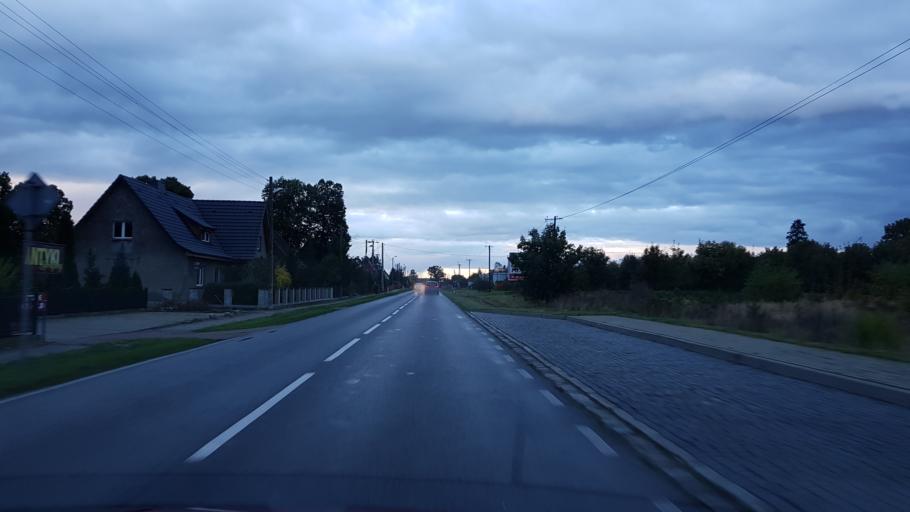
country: PL
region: Greater Poland Voivodeship
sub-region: Powiat pilski
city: Smilowo
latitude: 53.2182
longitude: 16.8670
